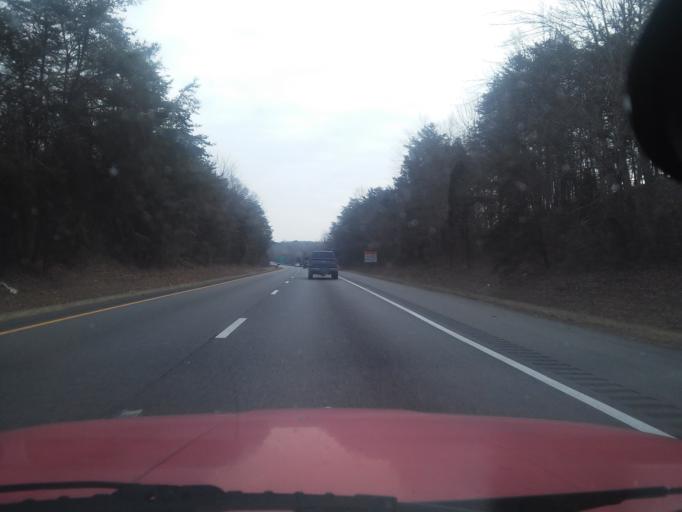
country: US
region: Virginia
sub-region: Fluvanna County
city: Lake Monticello
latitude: 38.0000
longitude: -78.3486
